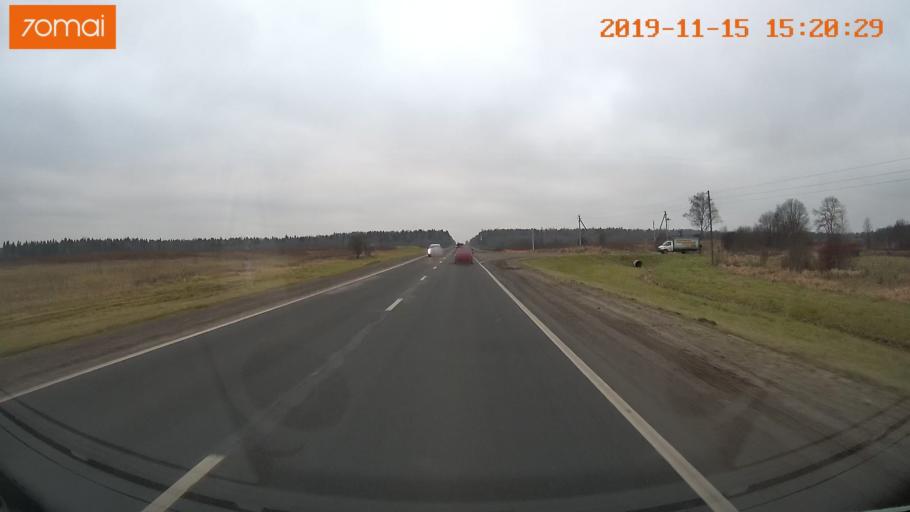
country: RU
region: Jaroslavl
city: Danilov
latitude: 58.2230
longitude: 40.1610
